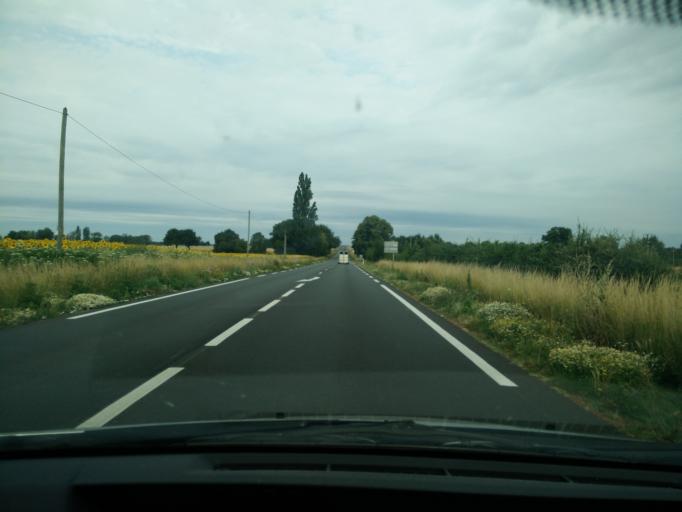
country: FR
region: Pays de la Loire
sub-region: Departement de Maine-et-Loire
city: Brissac-Quince
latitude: 47.3283
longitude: -0.4193
